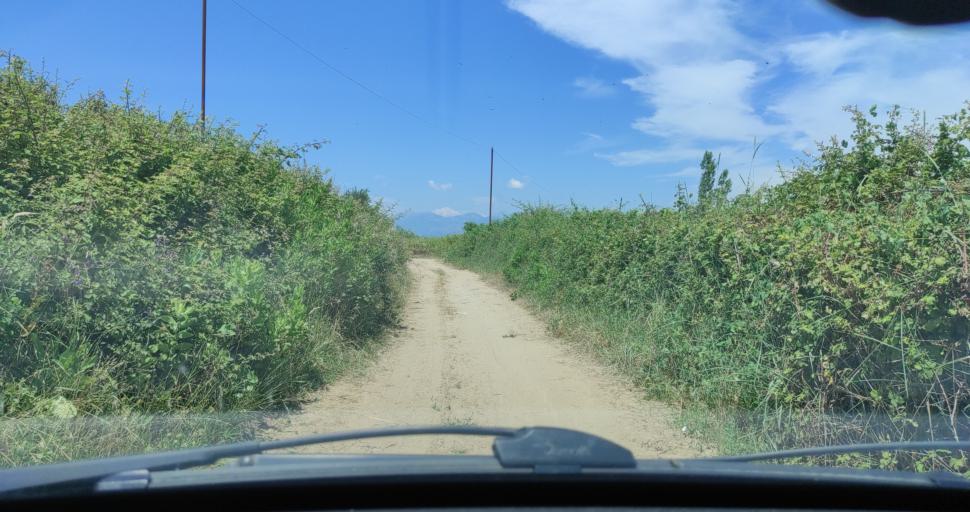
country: AL
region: Shkoder
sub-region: Rrethi i Shkodres
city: Velipoje
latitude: 41.8841
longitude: 19.3888
